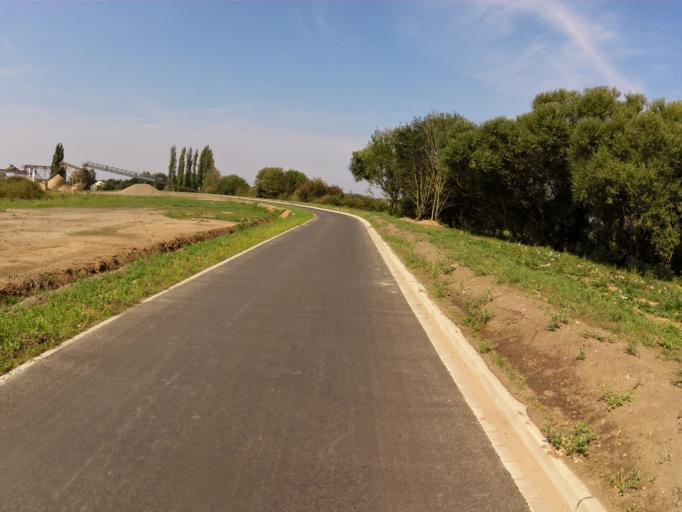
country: DE
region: Bremen
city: Bremen
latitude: 53.0231
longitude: 8.8726
